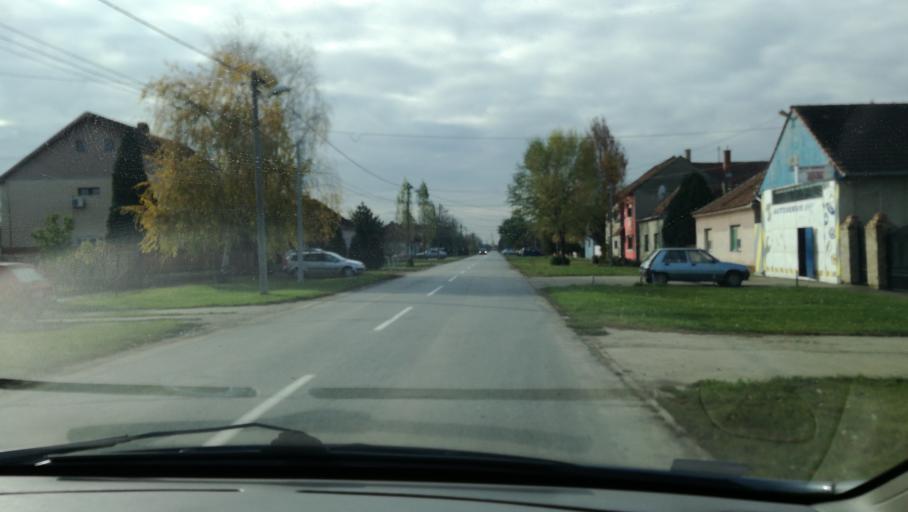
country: RS
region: Autonomna Pokrajina Vojvodina
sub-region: Severnobanatski Okrug
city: Kikinda
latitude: 45.8286
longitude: 20.4372
